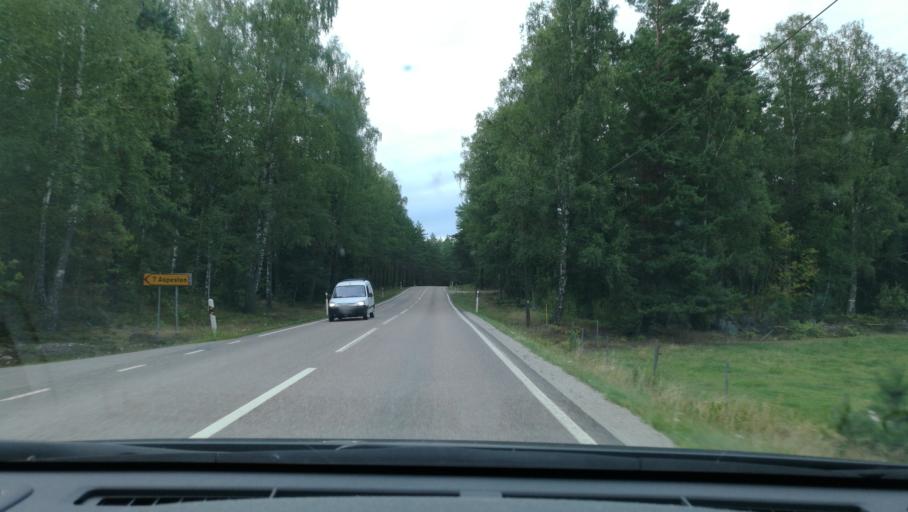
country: SE
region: Vaestmanland
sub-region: Kungsors Kommun
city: Kungsoer
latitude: 59.3355
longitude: 16.1114
